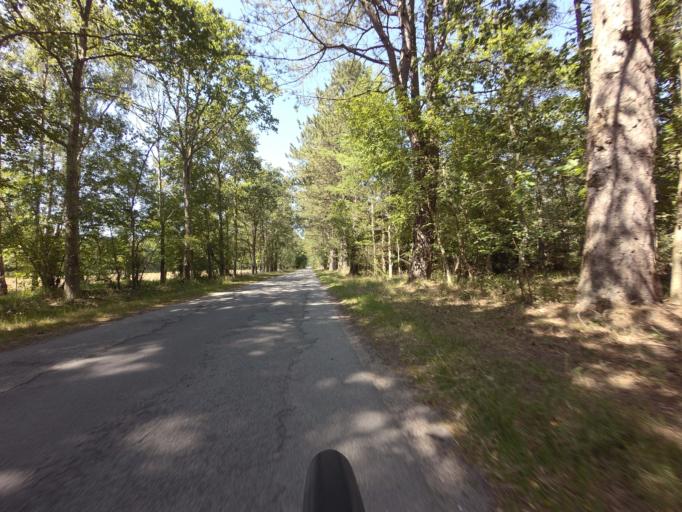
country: DK
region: North Denmark
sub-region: Laeso Kommune
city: Byrum
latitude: 57.2754
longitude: 11.0115
